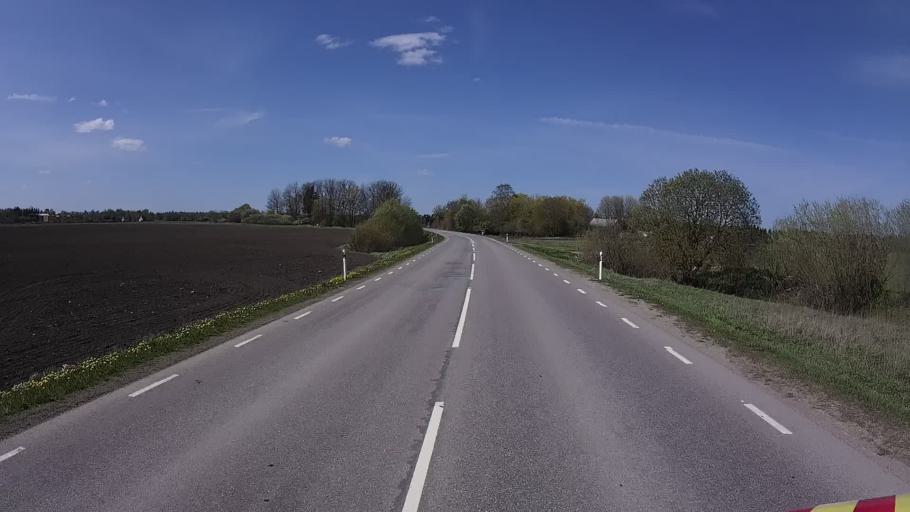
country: EE
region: Harju
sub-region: Keila linn
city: Keila
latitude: 59.2951
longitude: 24.3360
